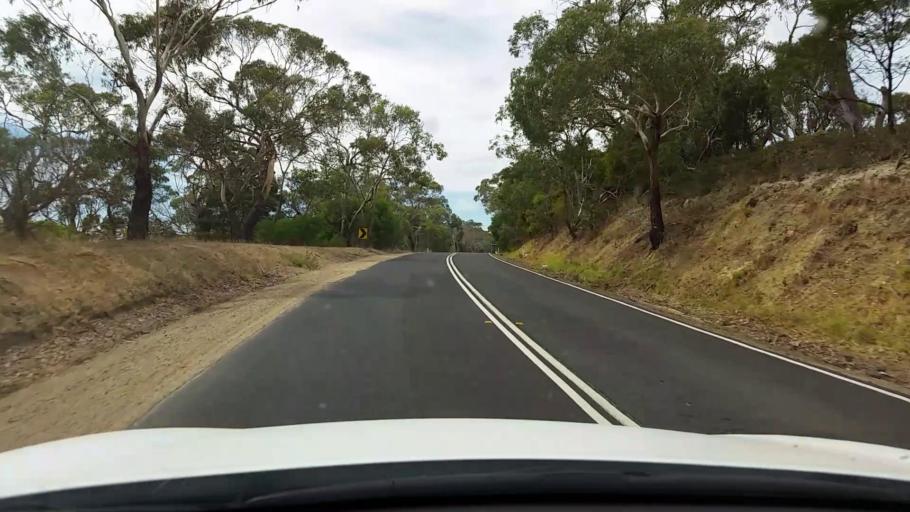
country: AU
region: Victoria
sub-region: Mornington Peninsula
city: Mount Martha
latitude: -38.2960
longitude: 145.0461
